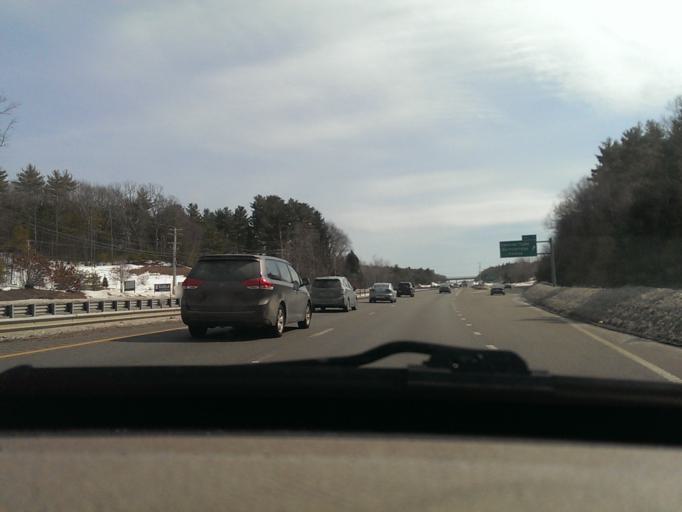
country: US
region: Massachusetts
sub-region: Worcester County
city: Sutton
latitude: 42.1563
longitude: -71.7296
